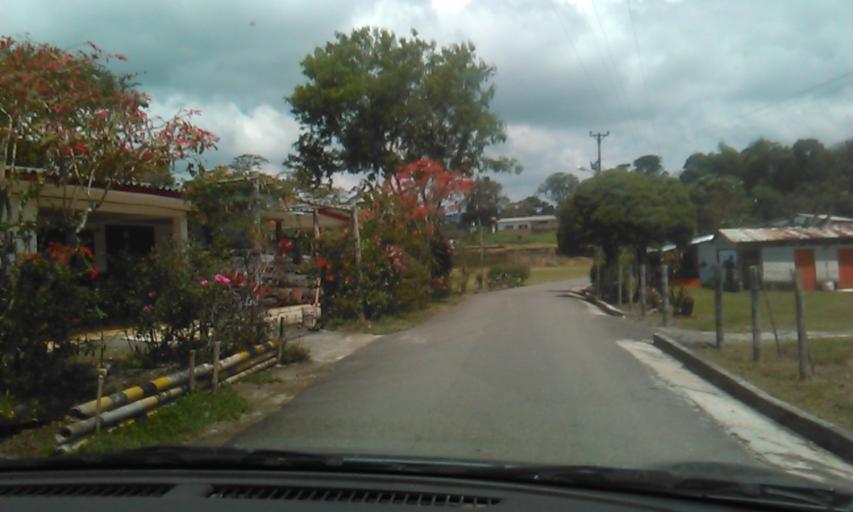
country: CO
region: Quindio
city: Circasia
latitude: 4.5952
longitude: -75.6503
